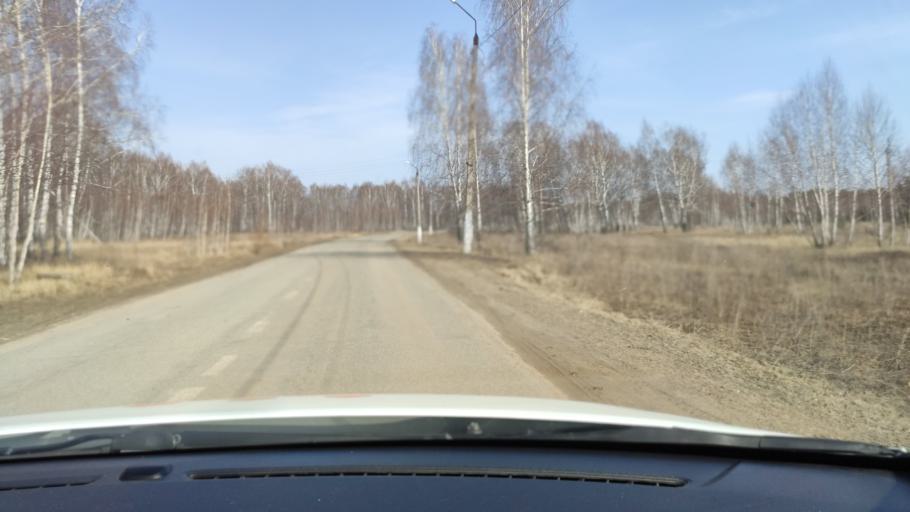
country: RU
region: Tatarstan
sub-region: Gorod Kazan'
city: Kazan
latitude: 55.6923
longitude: 49.1181
